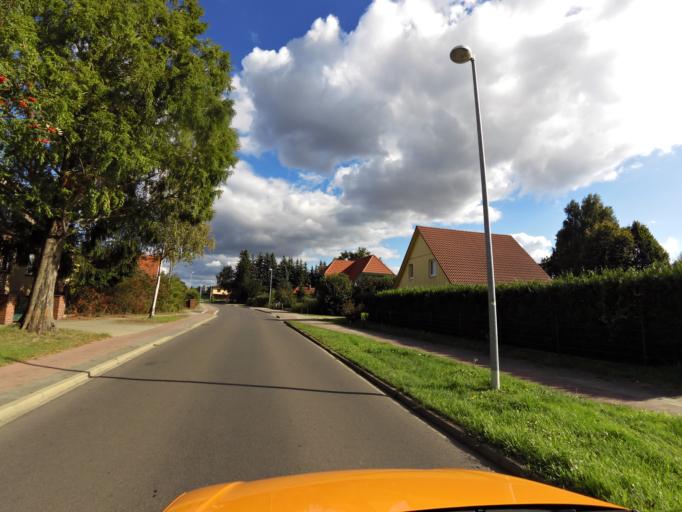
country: DE
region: Brandenburg
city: Luckenwalde
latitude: 52.0778
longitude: 13.1779
